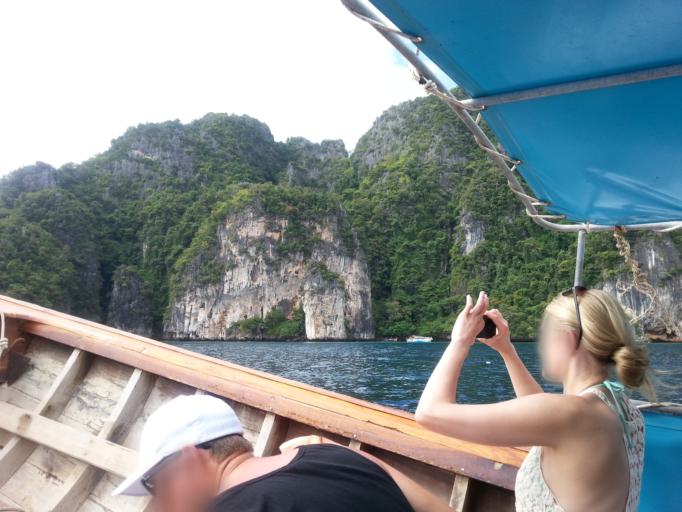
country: TH
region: Krabi
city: Saladan
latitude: 7.7222
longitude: 98.7719
